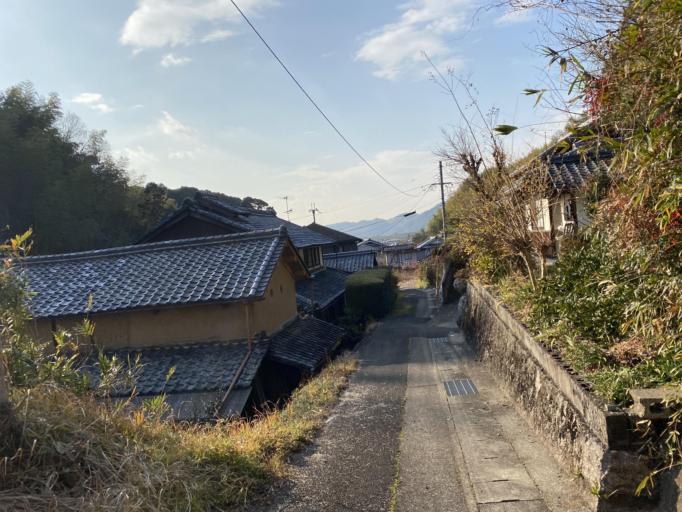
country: JP
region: Nara
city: Nara-shi
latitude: 34.7549
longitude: 135.8791
